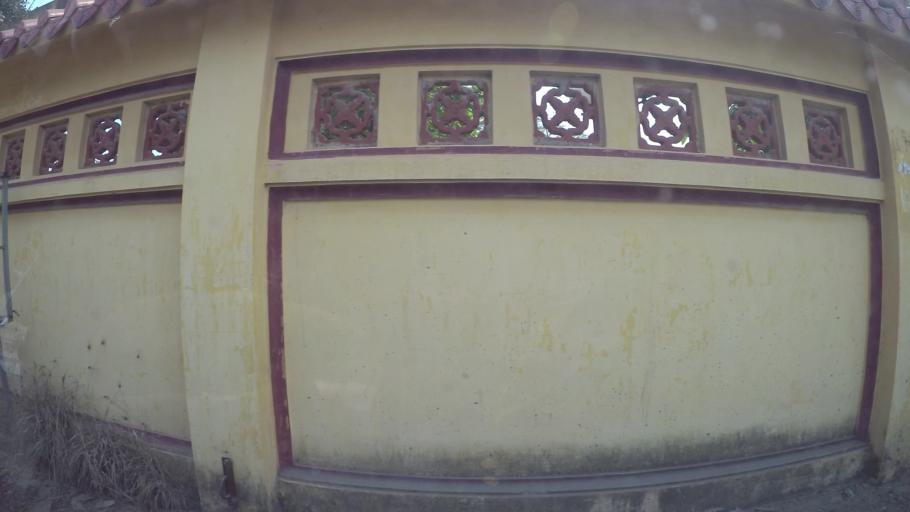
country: VN
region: Ha Noi
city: Van Dien
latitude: 20.9627
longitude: 105.8184
